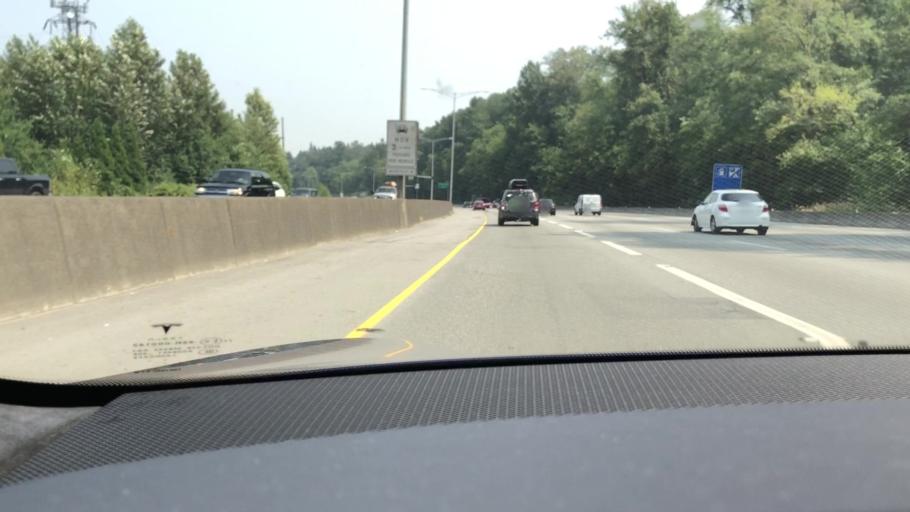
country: CA
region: British Columbia
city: Burnaby
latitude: 49.2363
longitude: -122.9333
